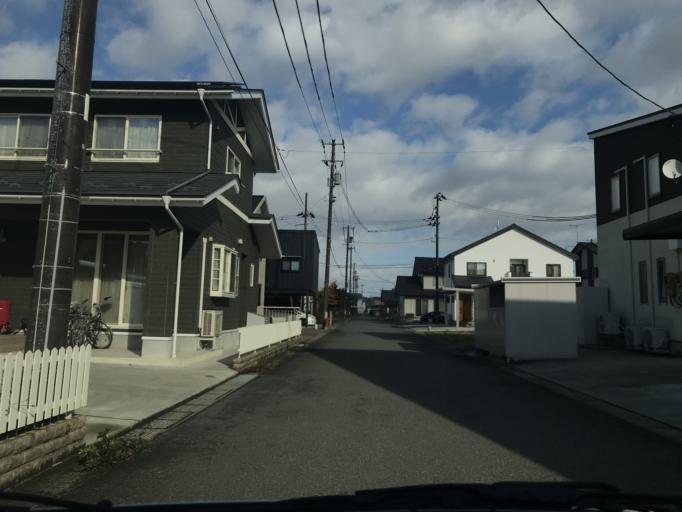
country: JP
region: Iwate
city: Mizusawa
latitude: 39.0523
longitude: 141.1261
